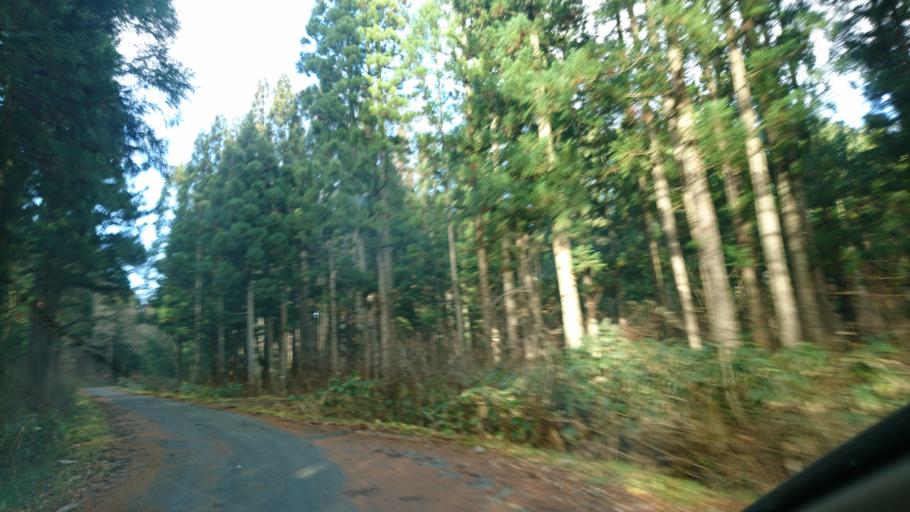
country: JP
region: Akita
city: Kakunodatemachi
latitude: 39.4660
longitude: 140.7904
